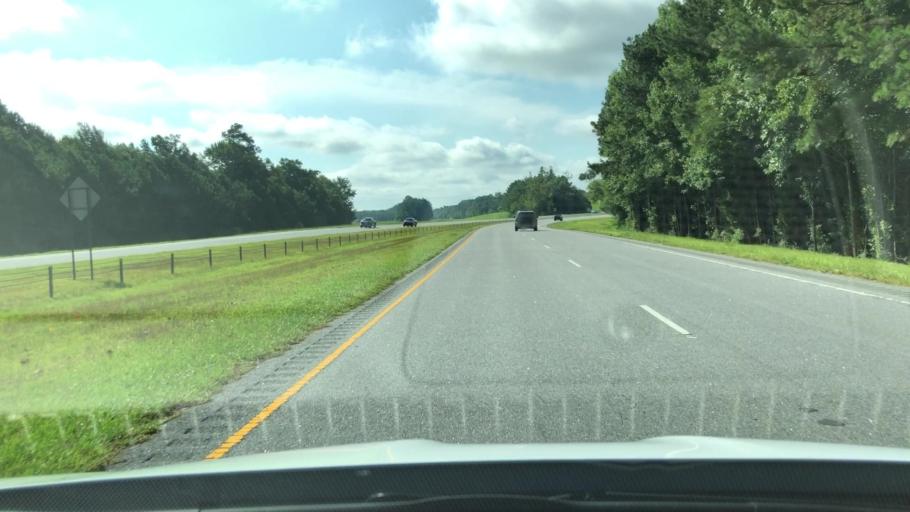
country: US
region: North Carolina
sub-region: Pasquotank County
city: Elizabeth City
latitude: 36.3805
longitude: -76.3116
